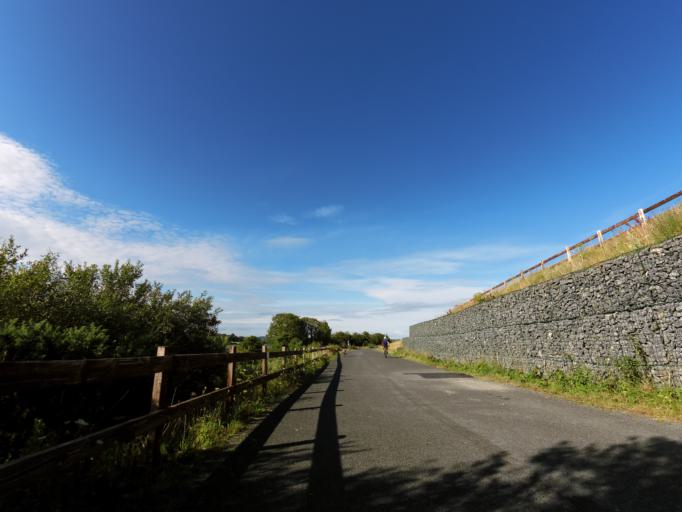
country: IE
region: Leinster
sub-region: Kilkenny
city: Mooncoin
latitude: 52.2565
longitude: -7.1894
